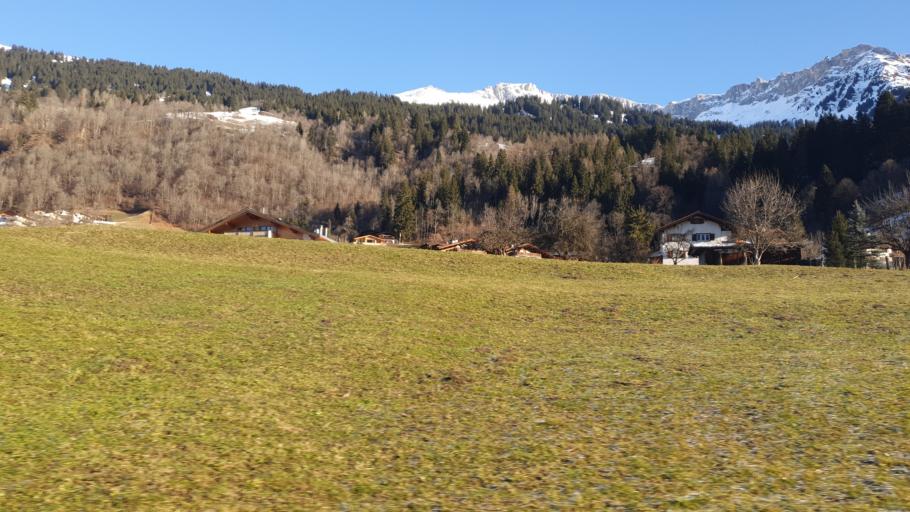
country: CH
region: Grisons
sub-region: Praettigau/Davos District
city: Klosters Serneus
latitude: 46.9063
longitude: 9.8128
